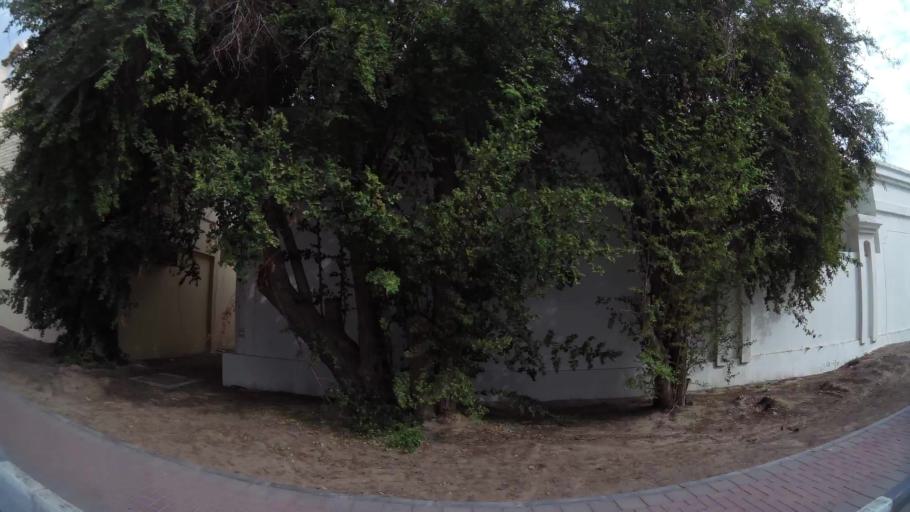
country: AE
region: Abu Dhabi
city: Al Ain
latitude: 24.2221
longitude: 55.7433
